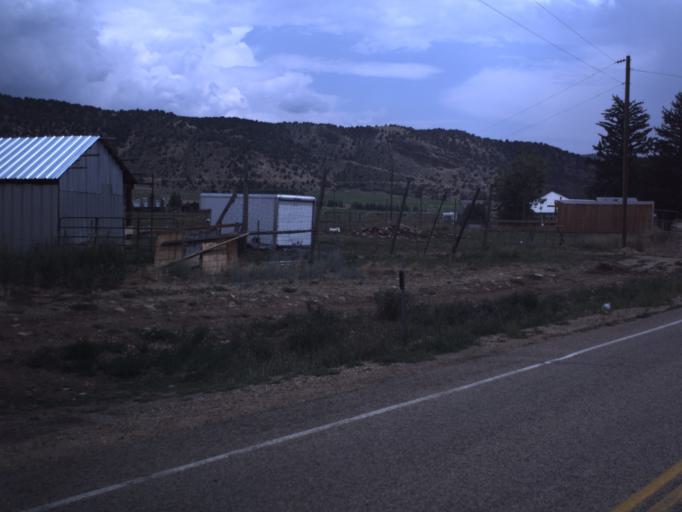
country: US
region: Utah
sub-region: Summit County
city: Francis
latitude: 40.4396
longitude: -110.8151
